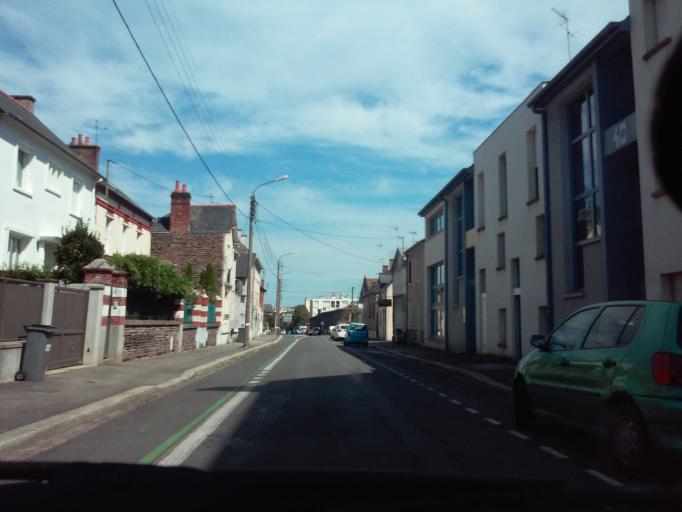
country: FR
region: Brittany
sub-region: Departement d'Ille-et-Vilaine
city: Rennes
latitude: 48.0971
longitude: -1.6863
